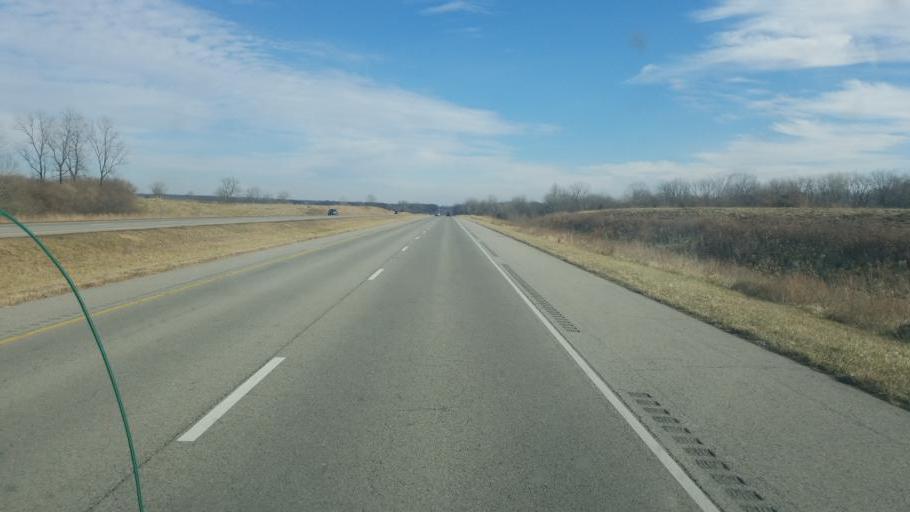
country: US
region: Illinois
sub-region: Saline County
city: Carrier Mills
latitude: 37.7302
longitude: -88.7765
